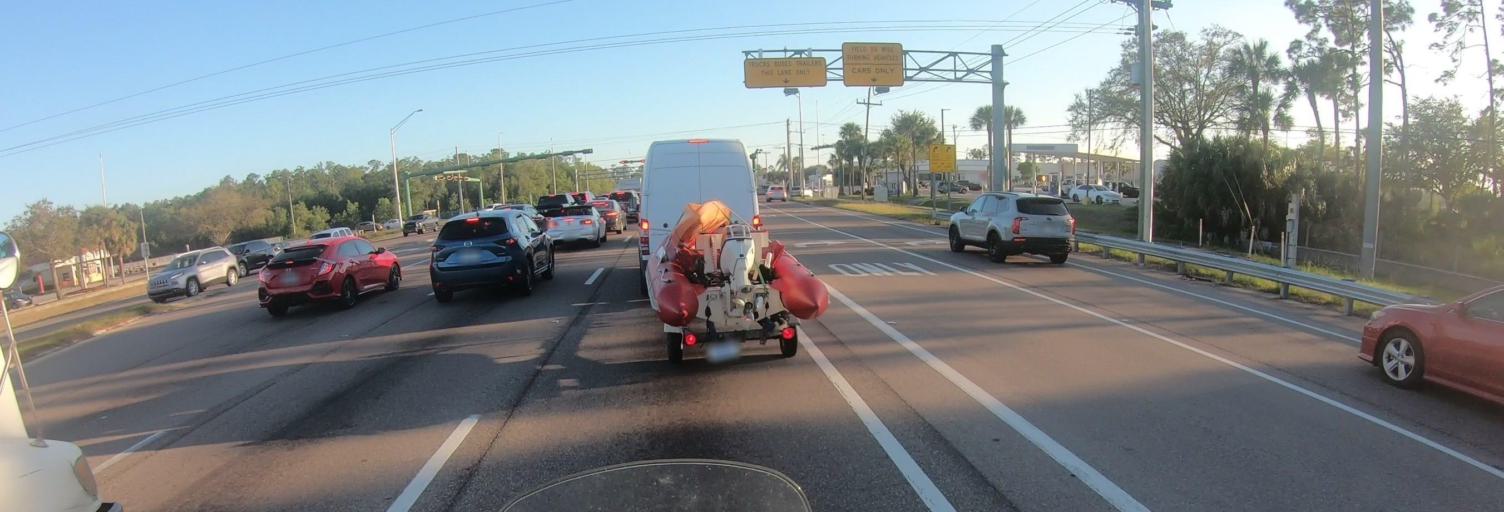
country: US
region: Florida
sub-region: Collier County
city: Golden Gate
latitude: 26.1540
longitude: -81.6881
